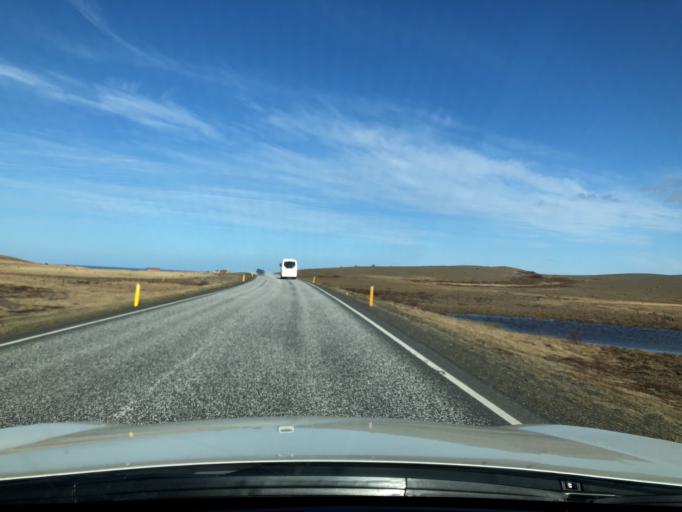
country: IS
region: West
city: Borgarnes
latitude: 64.4176
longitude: -21.9279
